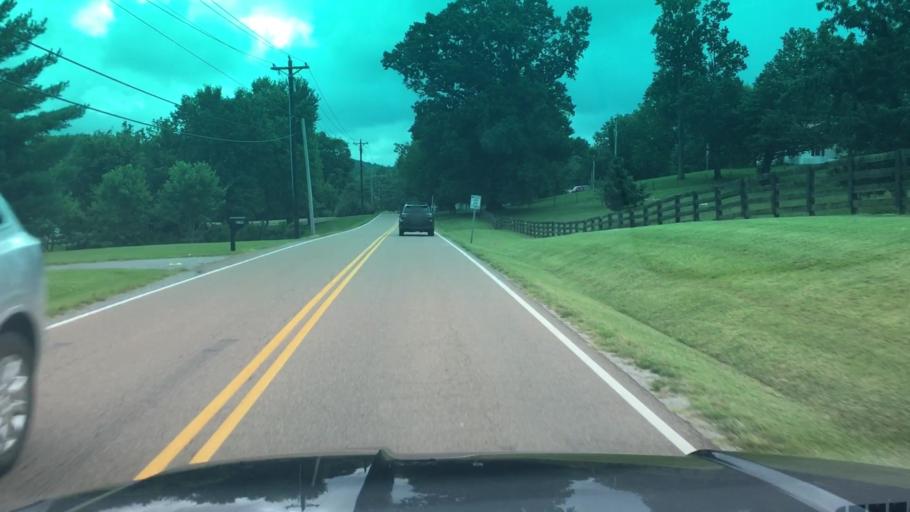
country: US
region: Tennessee
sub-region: Williamson County
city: Thompson's Station
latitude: 35.8078
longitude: -86.8552
